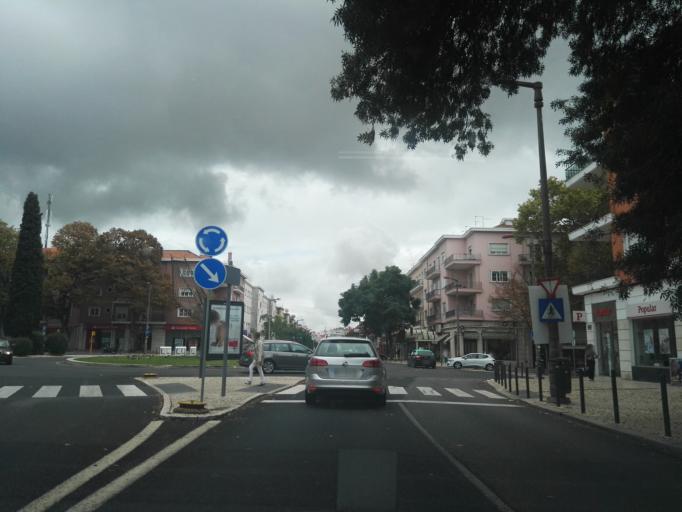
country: PT
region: Lisbon
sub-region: Lisbon
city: Lisbon
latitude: 38.7551
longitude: -9.1392
